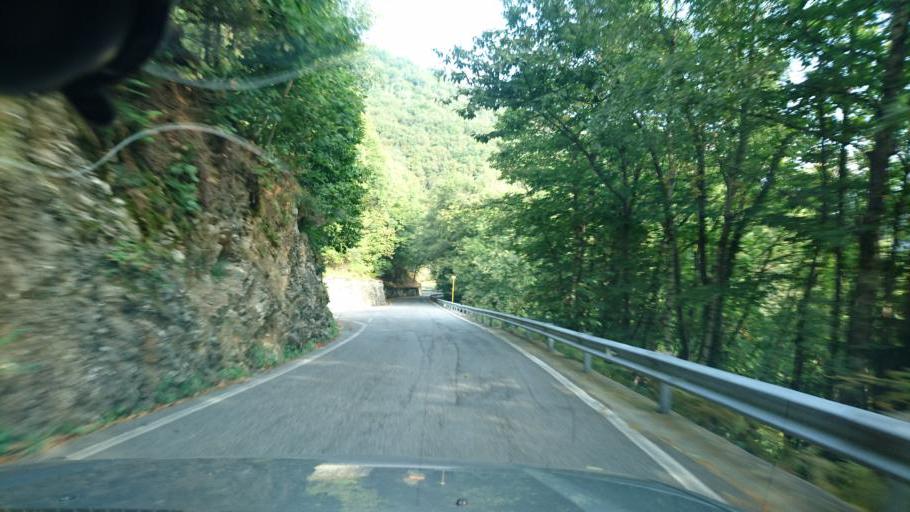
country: IT
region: Lombardy
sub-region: Provincia di Brescia
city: Paisco Loveno
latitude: 46.0894
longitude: 10.3060
